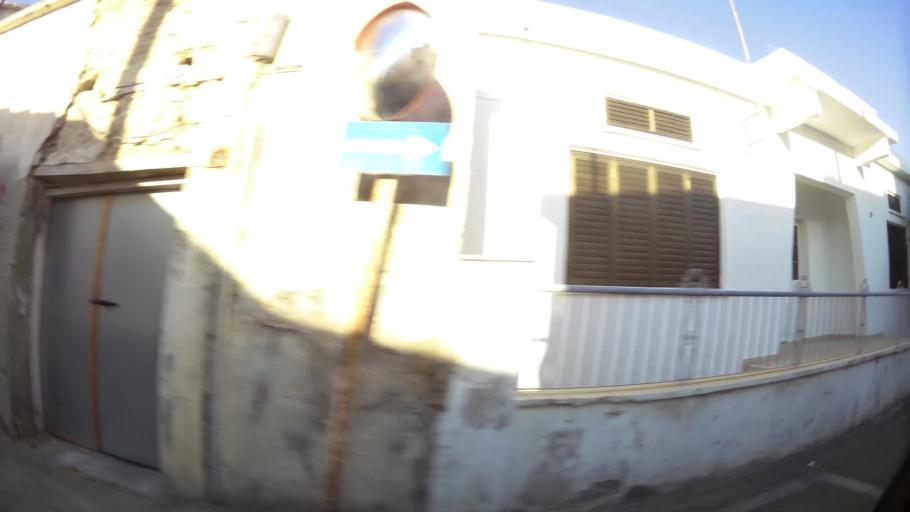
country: CY
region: Larnaka
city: Larnaca
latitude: 34.9092
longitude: 33.6358
